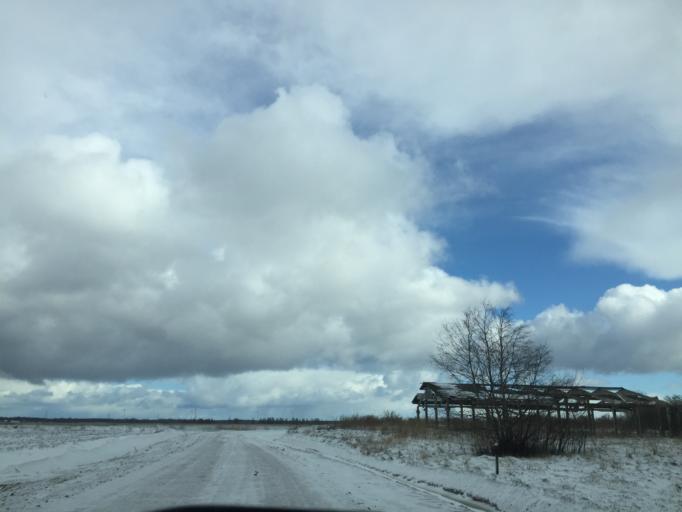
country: LV
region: Ventspils
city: Ventspils
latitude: 57.3711
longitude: 21.6289
